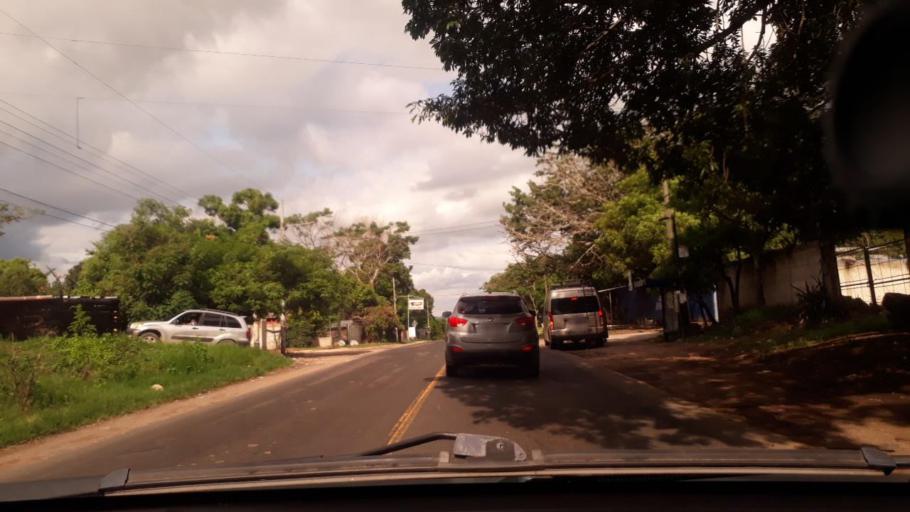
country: GT
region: Jutiapa
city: Quesada
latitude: 14.2772
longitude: -89.9841
